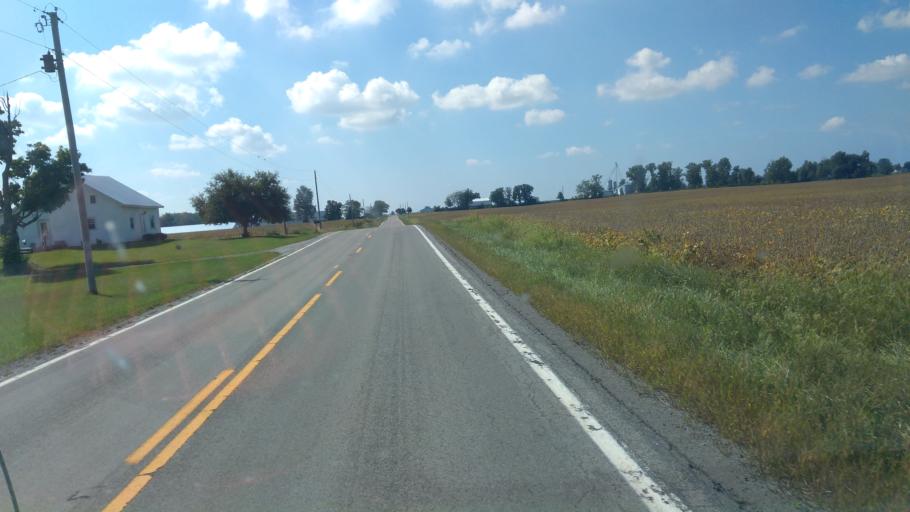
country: US
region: Ohio
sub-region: Logan County
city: Russells Point
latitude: 40.5869
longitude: -83.8472
